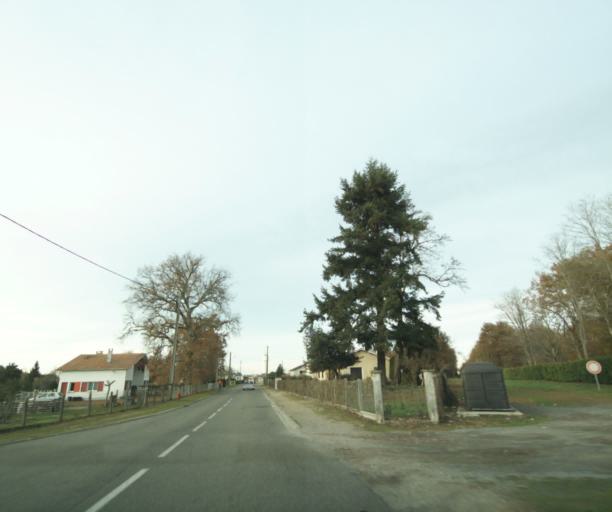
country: FR
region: Aquitaine
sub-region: Departement de la Gironde
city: Prechac
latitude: 44.2877
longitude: -0.2570
